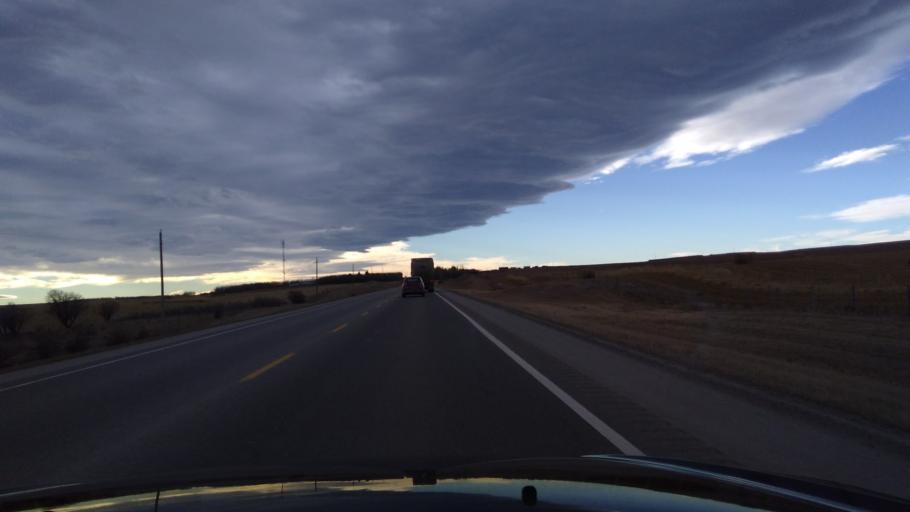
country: CA
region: Alberta
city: Cochrane
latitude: 51.1130
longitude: -114.4668
